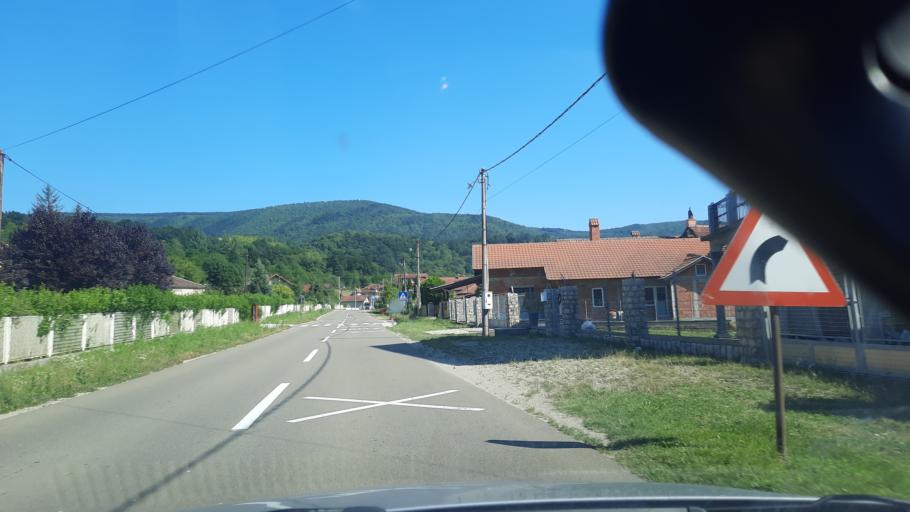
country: RS
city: Turija
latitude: 44.5245
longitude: 21.6378
